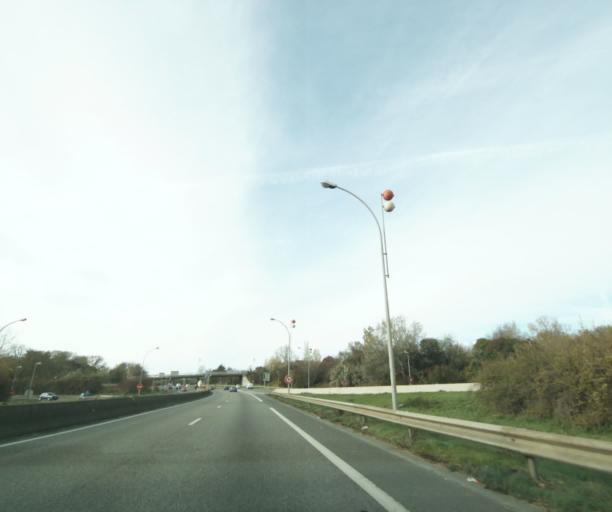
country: FR
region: Midi-Pyrenees
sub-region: Departement de la Haute-Garonne
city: Blagnac
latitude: 43.6104
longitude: 1.3850
